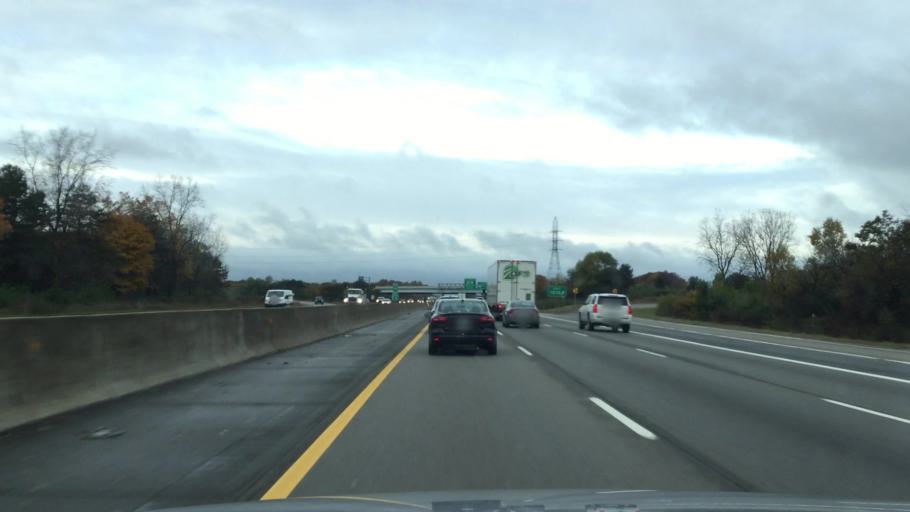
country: US
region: Michigan
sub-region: Washtenaw County
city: Ypsilanti
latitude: 42.2242
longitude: -83.6456
